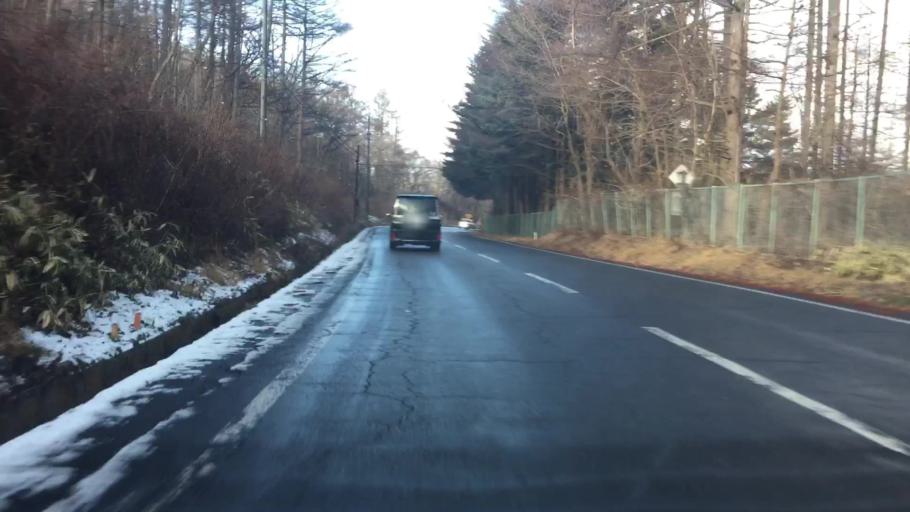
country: JP
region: Nagano
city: Saku
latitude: 36.3016
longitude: 138.6338
